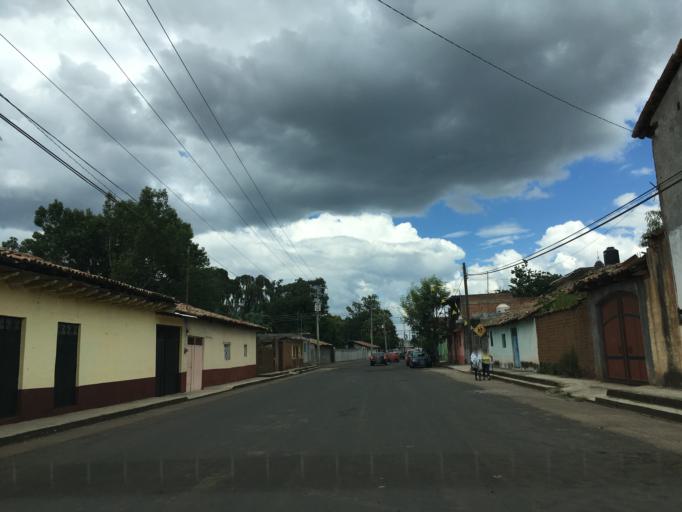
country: MX
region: Michoacan
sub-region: Jimenez
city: Copandaro (Copandaro del Cuatro)
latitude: 19.8199
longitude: -101.6804
